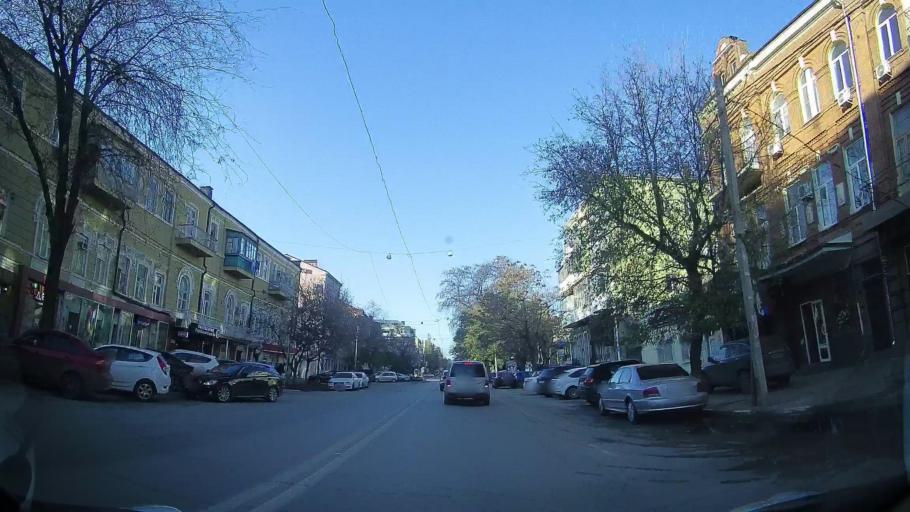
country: RU
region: Rostov
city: Rostov-na-Donu
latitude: 47.2248
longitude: 39.7206
